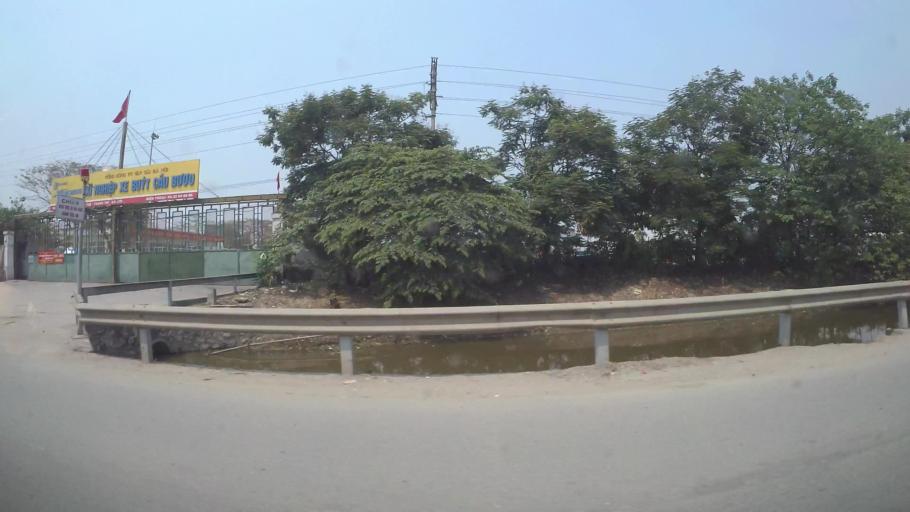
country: VN
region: Ha Noi
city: Van Dien
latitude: 20.9546
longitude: 105.8127
